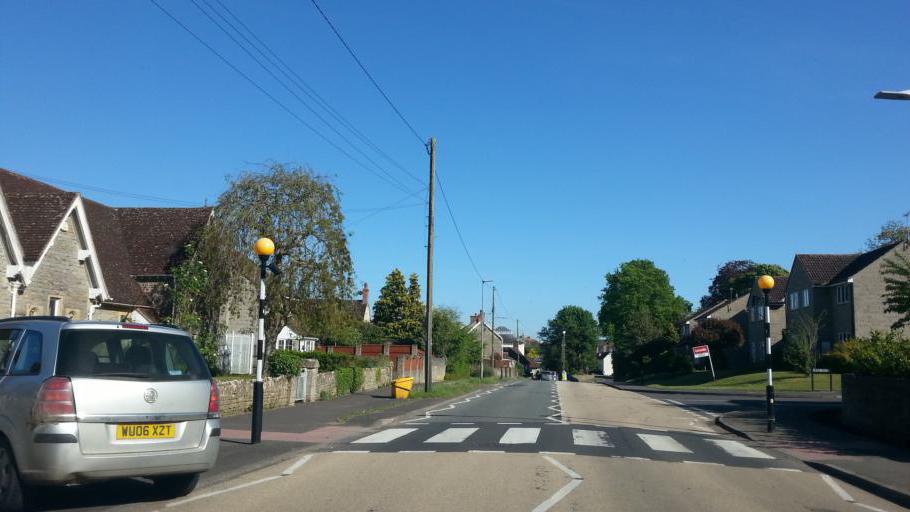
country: GB
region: England
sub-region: Dorset
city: Stalbridge
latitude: 50.9790
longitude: -2.3969
